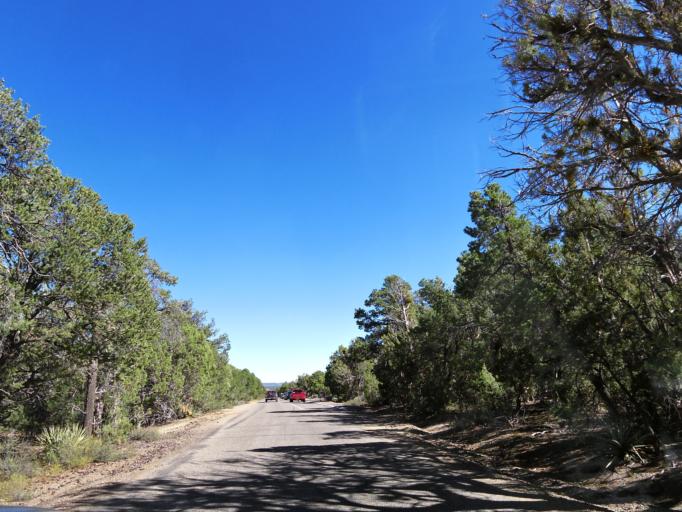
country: US
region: Colorado
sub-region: Montezuma County
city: Cortez
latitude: 37.1642
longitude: -108.4846
